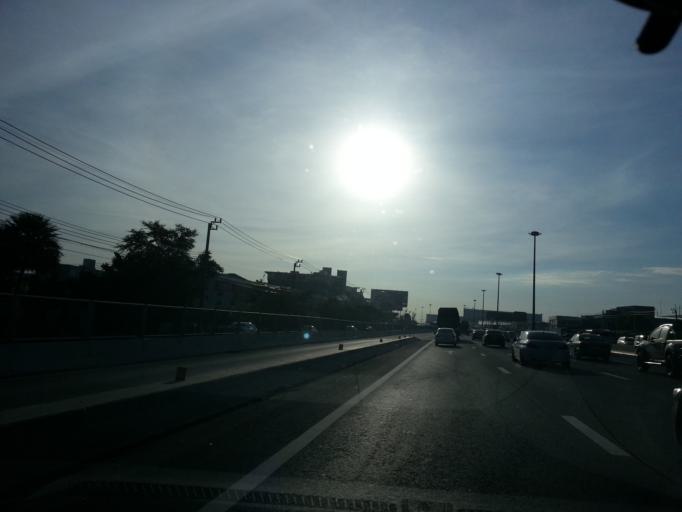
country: TH
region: Bangkok
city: Lat Krabang
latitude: 13.7298
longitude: 100.7297
